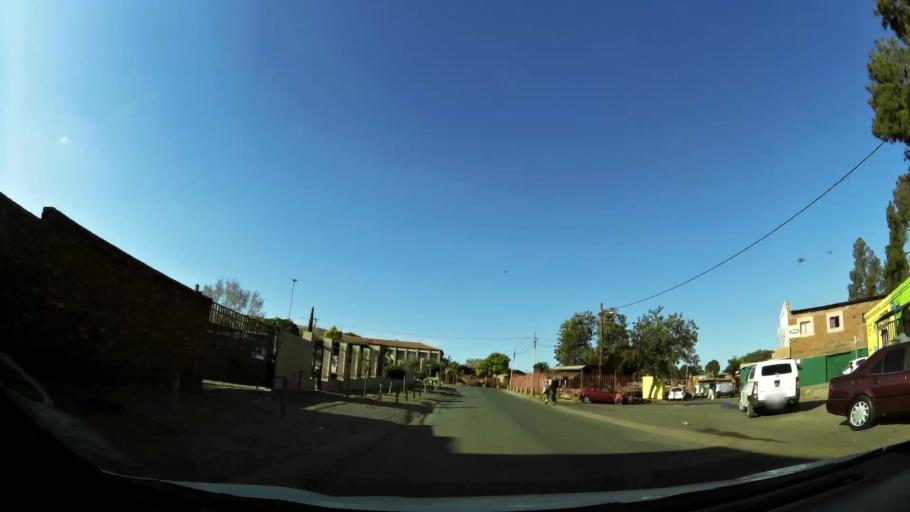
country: ZA
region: Gauteng
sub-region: City of Tshwane Metropolitan Municipality
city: Cullinan
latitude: -25.7068
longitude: 28.3741
